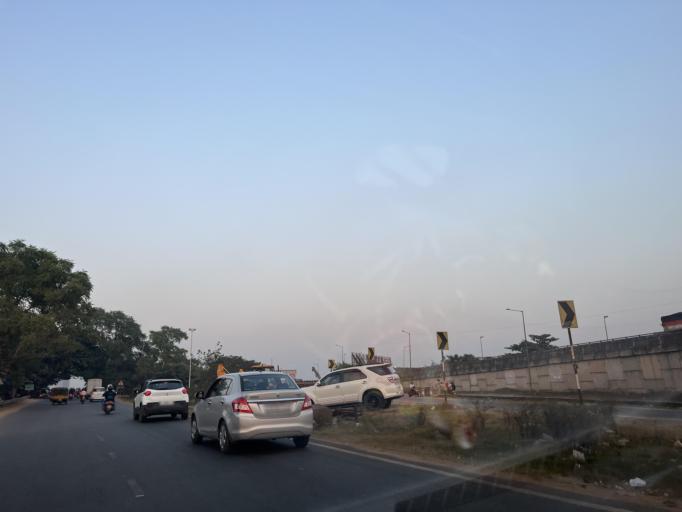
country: IN
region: Odisha
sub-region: Khordha
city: Bhubaneshwar
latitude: 20.3101
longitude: 85.8730
